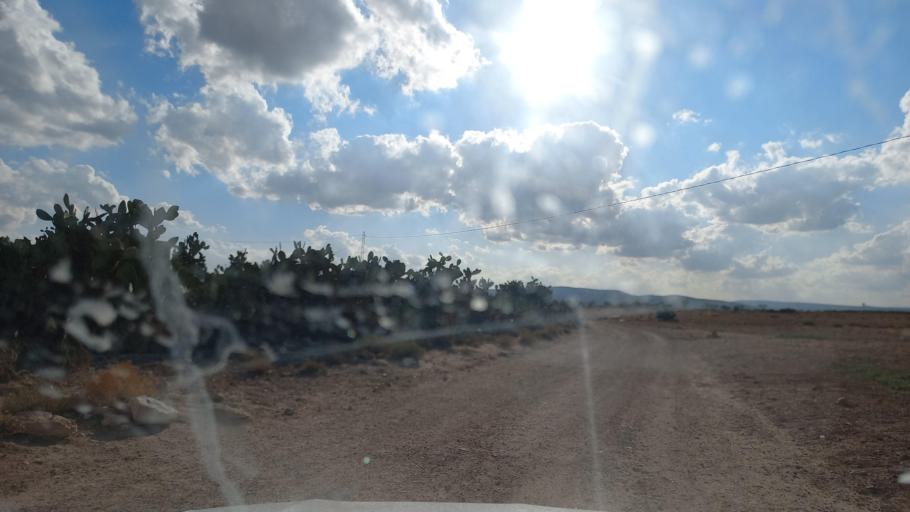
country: TN
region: Al Qasrayn
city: Sbiba
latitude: 35.3892
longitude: 9.0671
